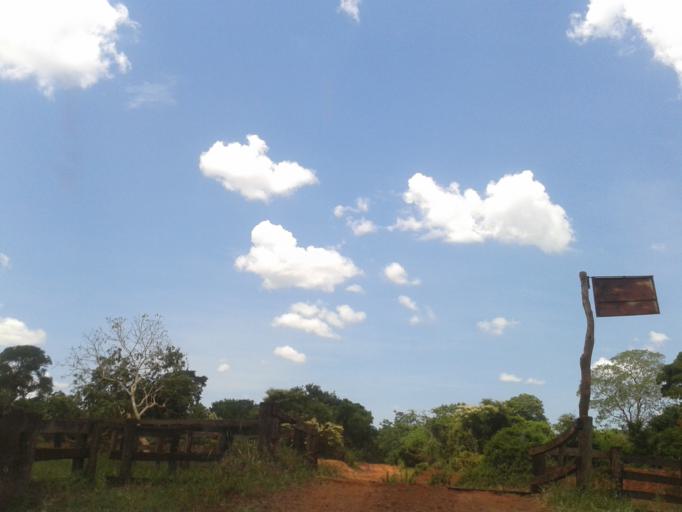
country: BR
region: Minas Gerais
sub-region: Santa Vitoria
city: Santa Vitoria
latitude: -19.2060
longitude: -50.3958
